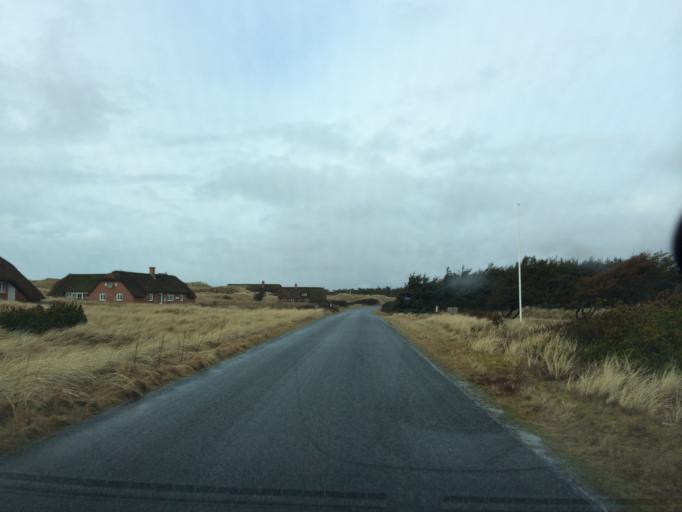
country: DK
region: Central Jutland
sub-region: Holstebro Kommune
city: Ulfborg
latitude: 56.2505
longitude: 8.1355
